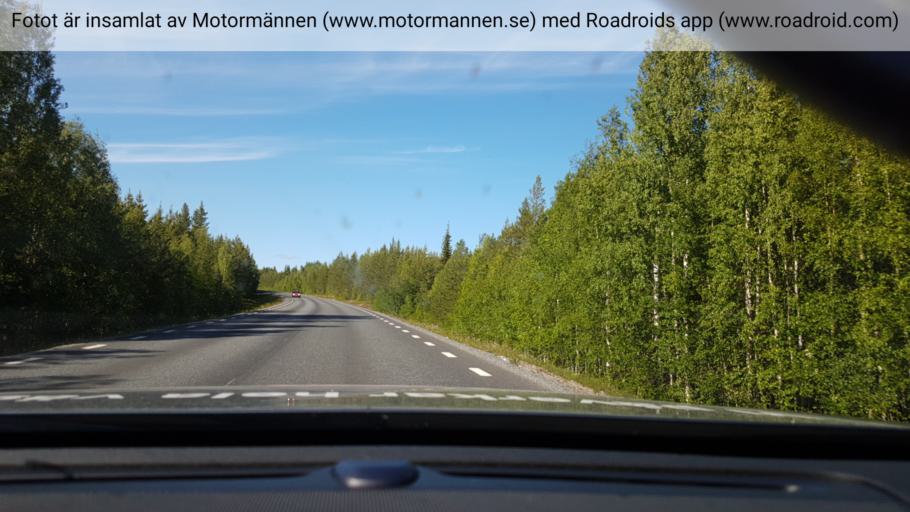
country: SE
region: Vaesterbotten
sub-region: Lycksele Kommun
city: Lycksele
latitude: 64.7823
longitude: 18.7353
